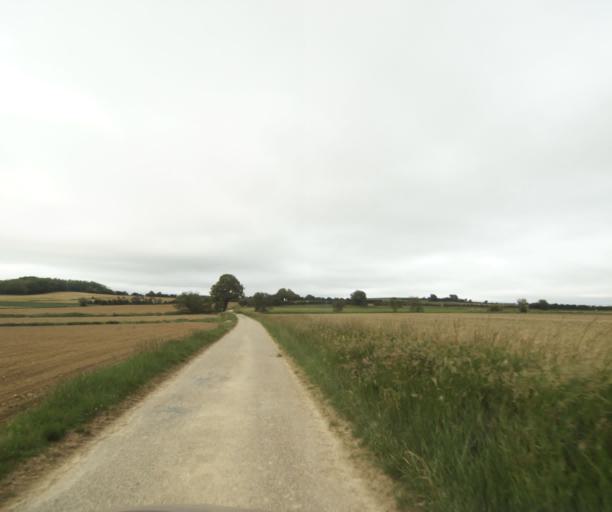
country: FR
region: Rhone-Alpes
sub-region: Departement de l'Ain
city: Miribel
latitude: 45.8411
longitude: 4.9440
